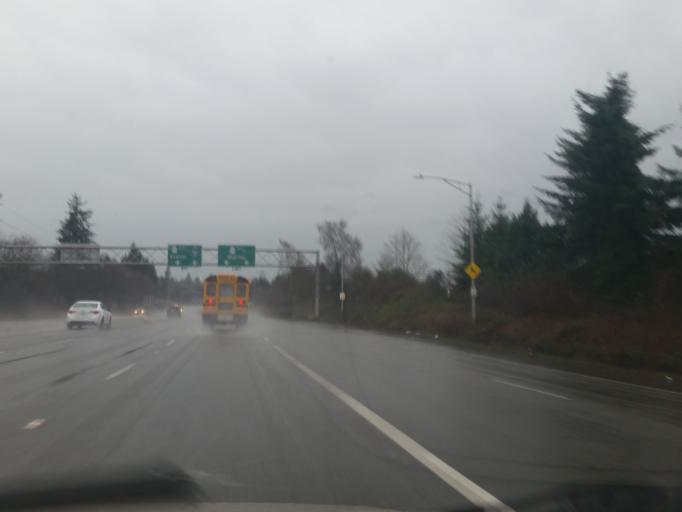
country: US
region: Washington
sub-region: Snohomish County
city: Mukilteo
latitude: 47.9284
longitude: -122.2608
